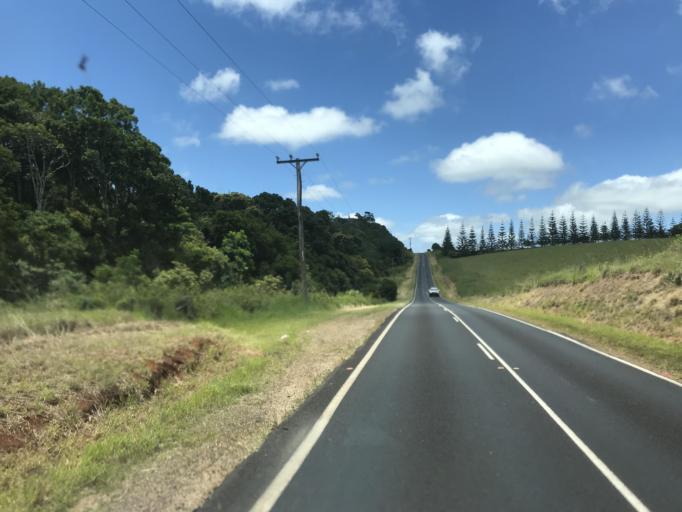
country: AU
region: Queensland
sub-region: Tablelands
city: Ravenshoe
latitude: -17.5021
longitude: 145.4765
